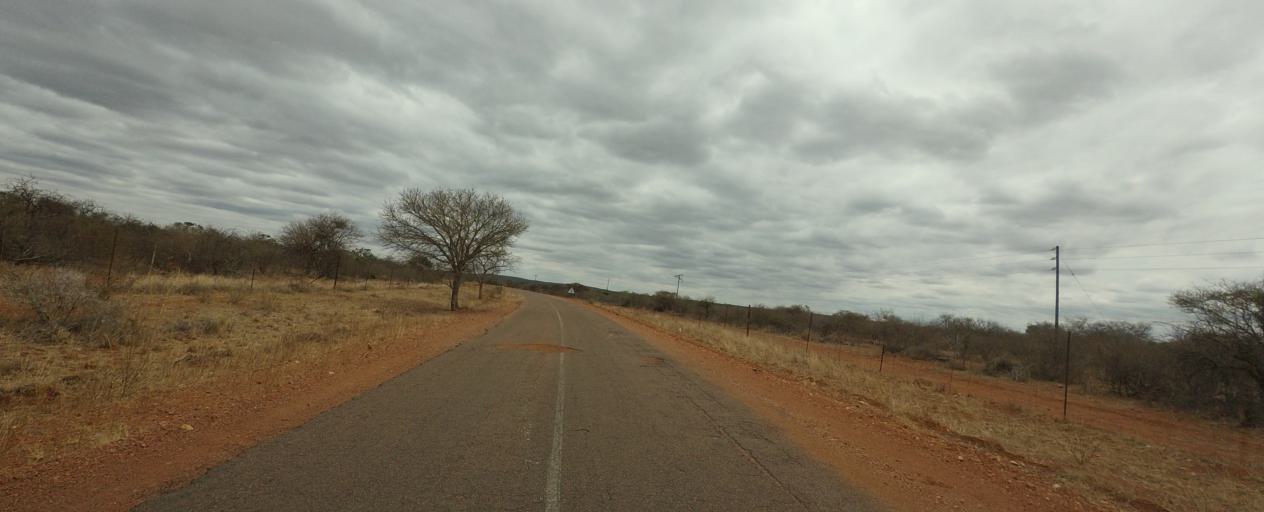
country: BW
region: Central
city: Mathathane
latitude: -22.7389
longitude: 28.4598
